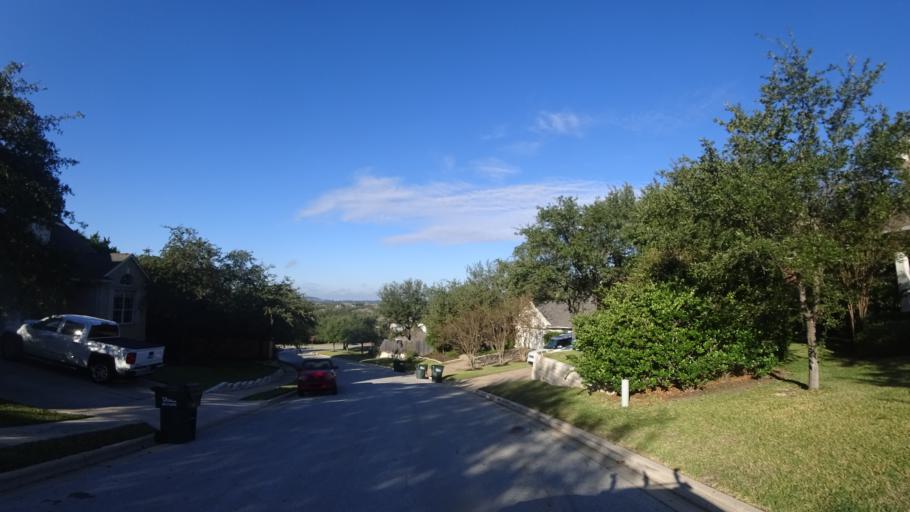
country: US
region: Texas
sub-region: Travis County
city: Hudson Bend
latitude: 30.3701
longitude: -97.8997
